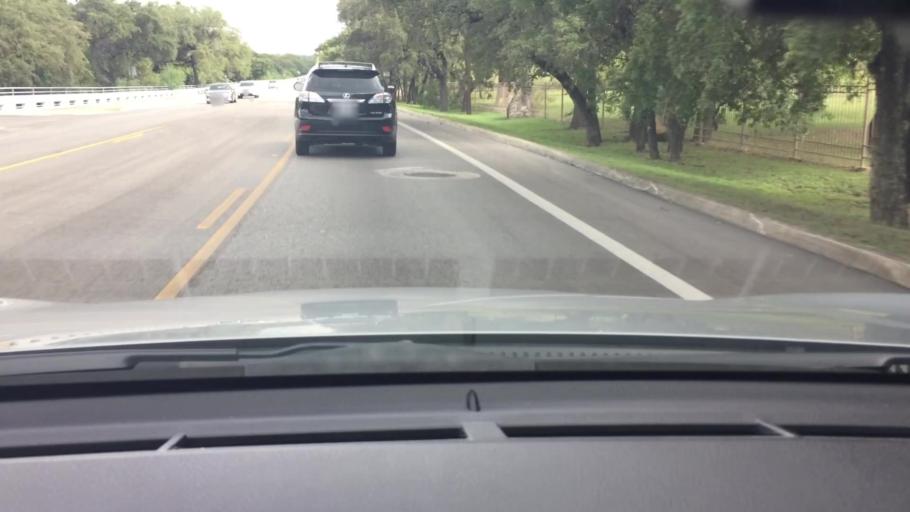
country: US
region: Texas
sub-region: Bexar County
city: Shavano Park
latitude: 29.5551
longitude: -98.5465
